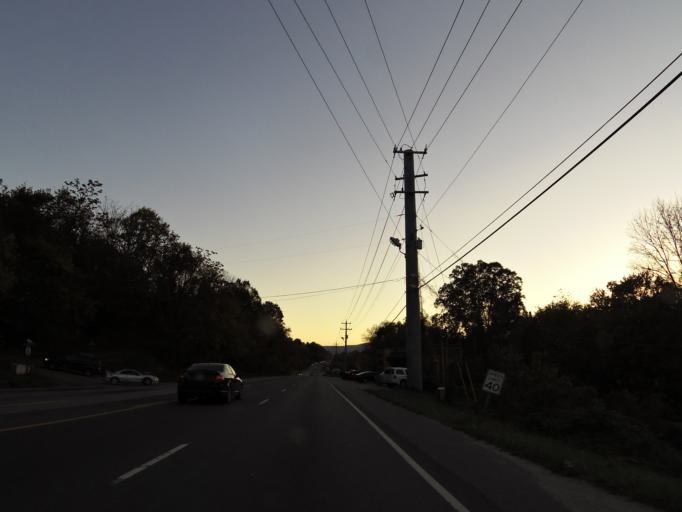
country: US
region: Tennessee
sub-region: Campbell County
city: Hunter
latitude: 36.3630
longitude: -84.1398
